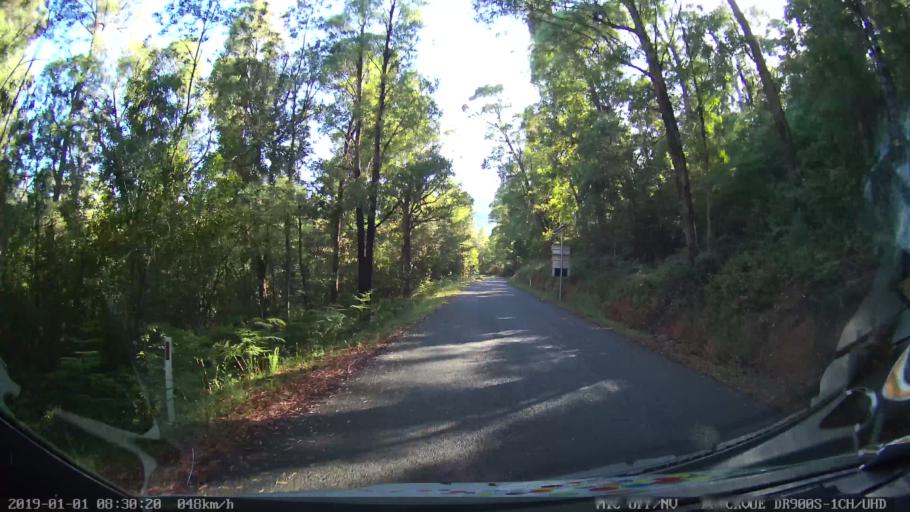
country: AU
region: New South Wales
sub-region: Snowy River
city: Jindabyne
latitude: -36.3763
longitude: 148.1974
